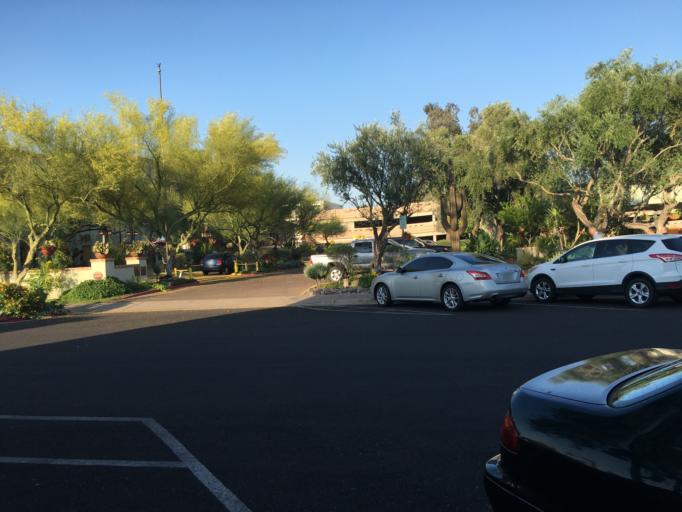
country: US
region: Arizona
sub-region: Maricopa County
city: Scottsdale
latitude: 33.4925
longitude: -111.9246
